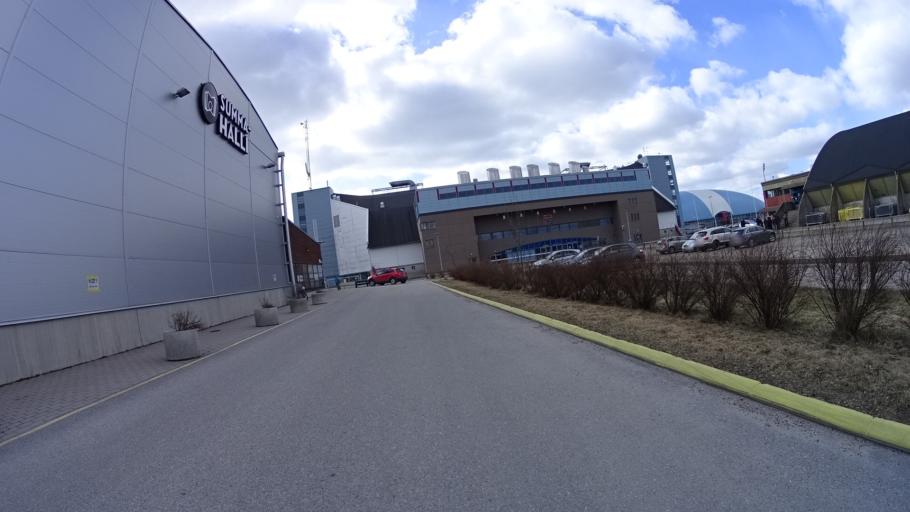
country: FI
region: Uusimaa
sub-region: Helsinki
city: Koukkuniemi
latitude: 60.1789
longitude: 24.7865
